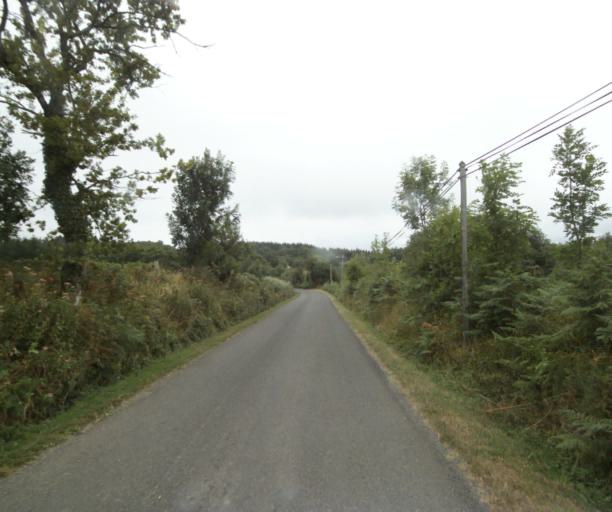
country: FR
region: Midi-Pyrenees
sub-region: Departement du Tarn
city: Soreze
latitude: 43.4086
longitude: 2.0561
